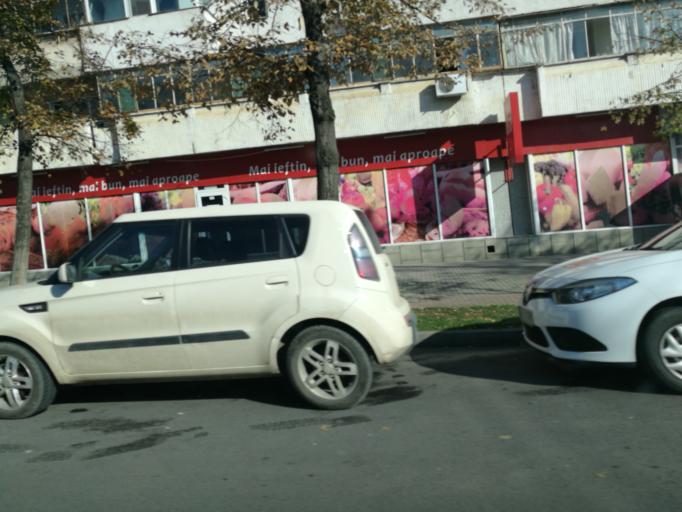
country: RO
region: Iasi
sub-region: Comuna Miroslava
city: Miroslava
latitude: 47.1743
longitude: 27.5533
